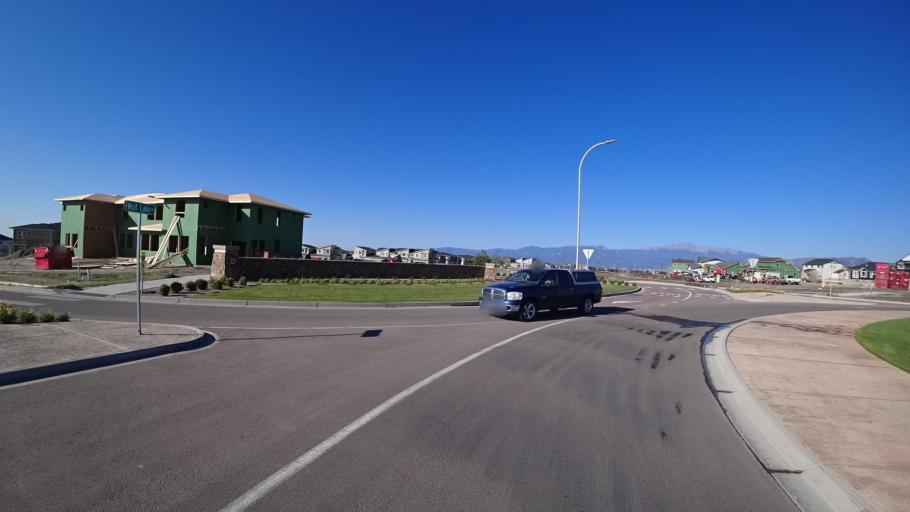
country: US
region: Colorado
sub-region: El Paso County
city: Black Forest
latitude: 38.9752
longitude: -104.7162
